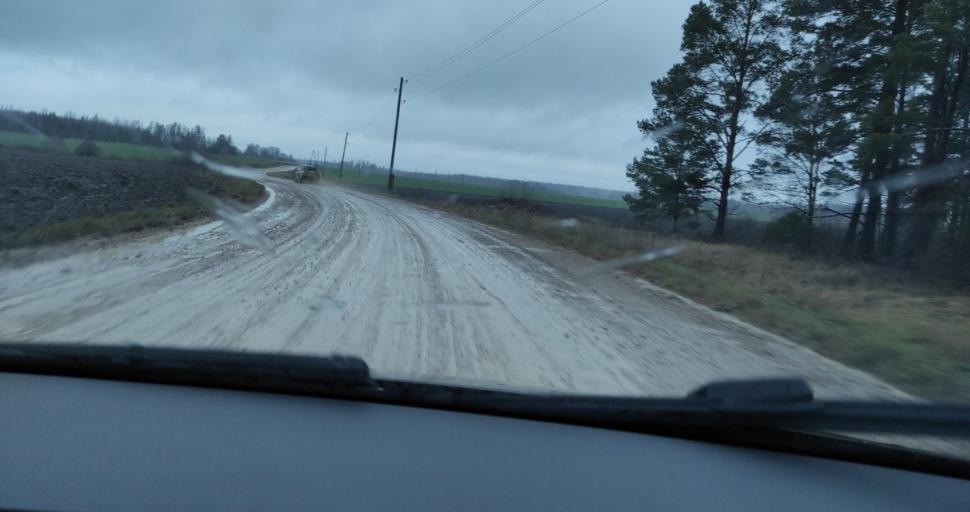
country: LV
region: Skrunda
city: Skrunda
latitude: 56.6885
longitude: 22.2225
